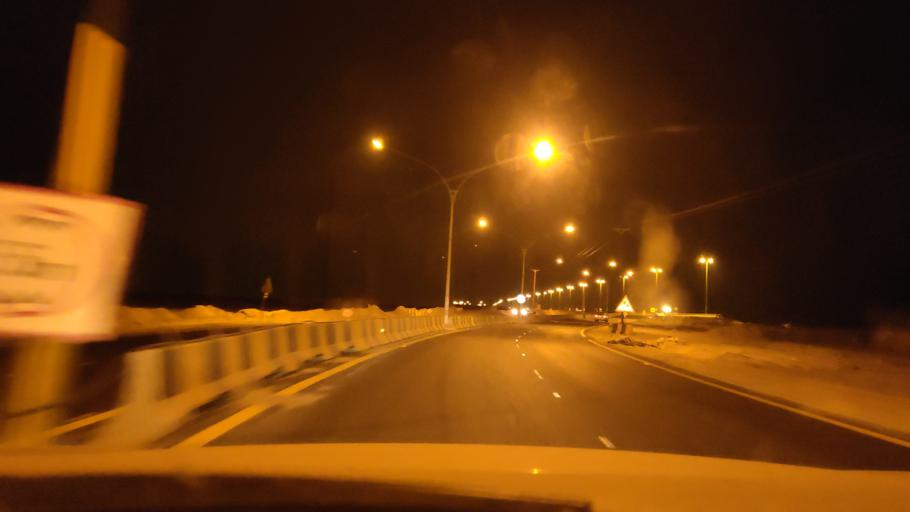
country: KW
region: Al Ahmadi
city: Al Ahmadi
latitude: 28.9008
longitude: 48.0902
